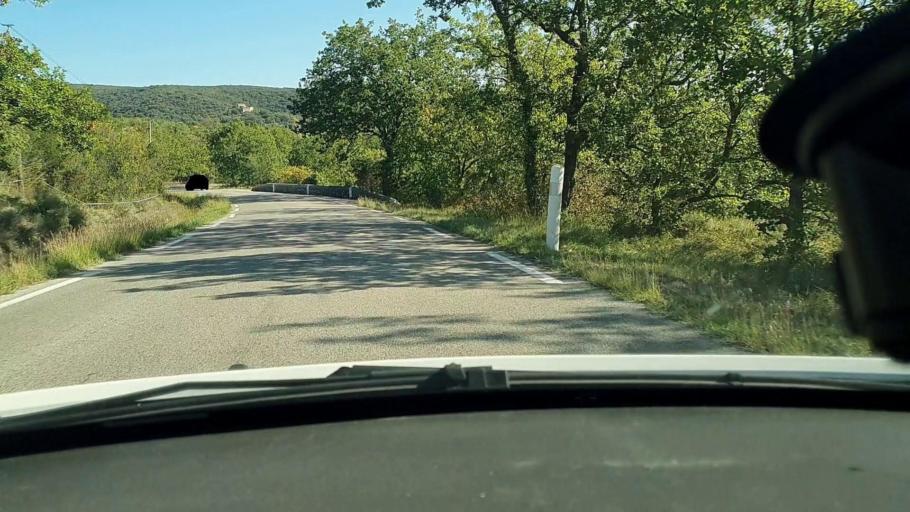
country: FR
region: Languedoc-Roussillon
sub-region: Departement du Gard
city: Saint-Julien-de-Peyrolas
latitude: 44.2957
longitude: 4.4909
